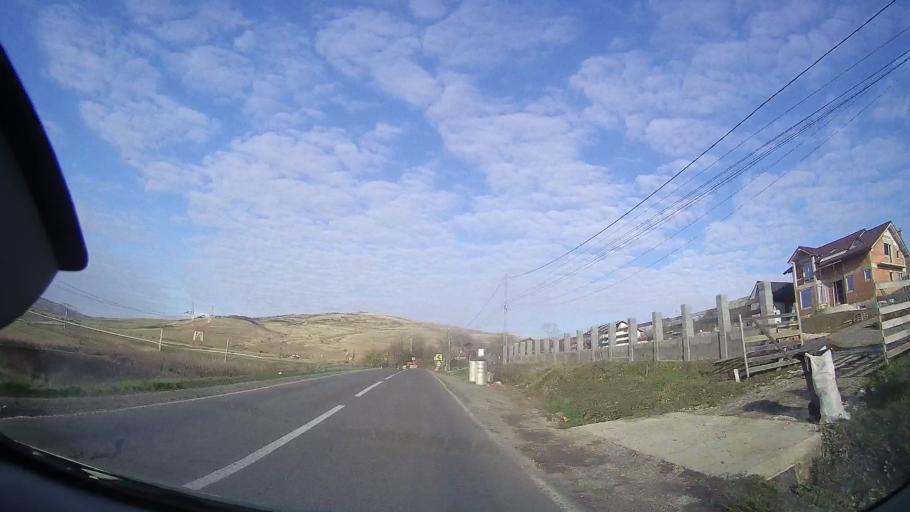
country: RO
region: Cluj
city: Caianu Mic
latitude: 46.8106
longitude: 23.8727
